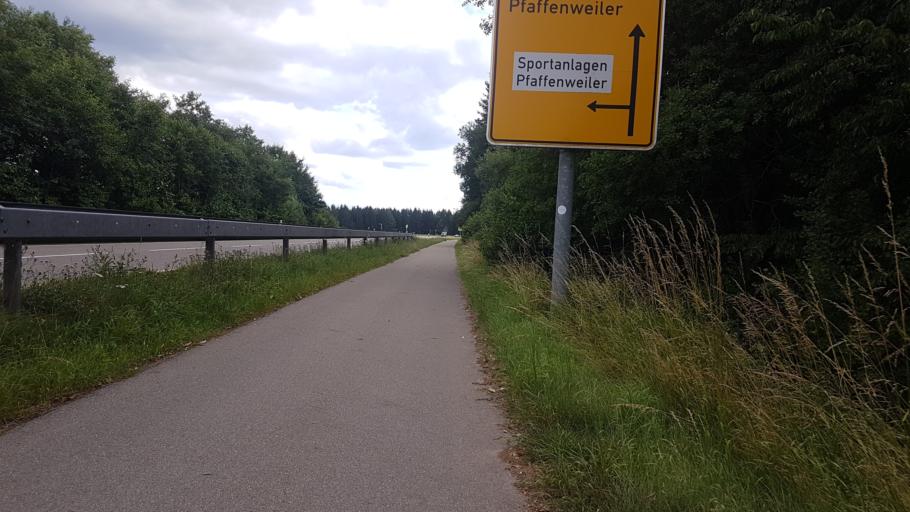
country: DE
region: Baden-Wuerttemberg
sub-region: Freiburg Region
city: Monchweiler
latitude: 48.0480
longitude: 8.4206
